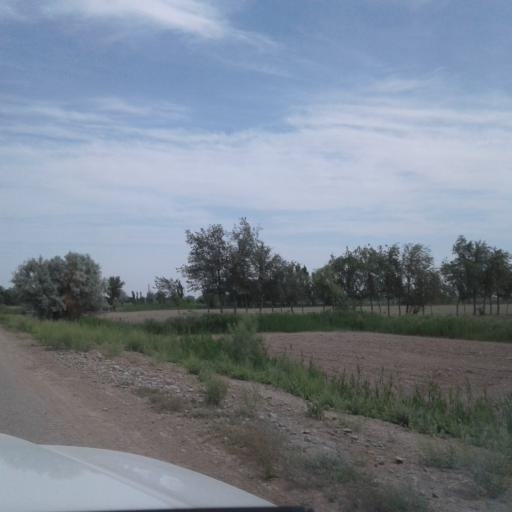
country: TM
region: Dasoguz
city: Tagta
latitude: 41.5596
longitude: 59.8127
